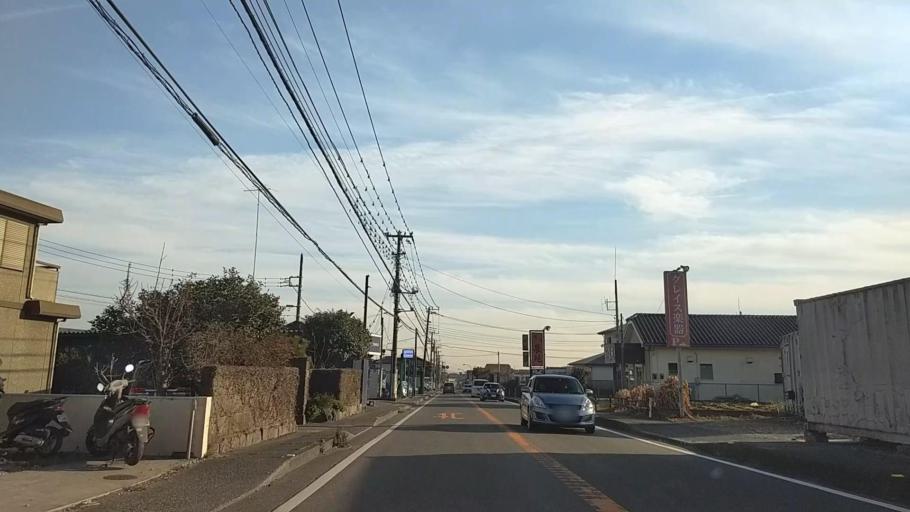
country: JP
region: Kanagawa
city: Zama
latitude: 35.5020
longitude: 139.3116
